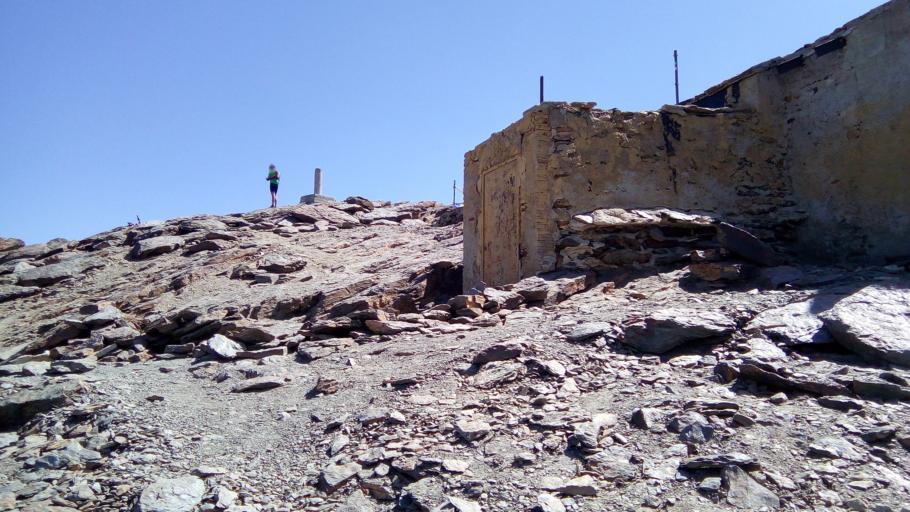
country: ES
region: Andalusia
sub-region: Provincia de Granada
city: Capileira
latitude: 37.0558
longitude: -3.3660
